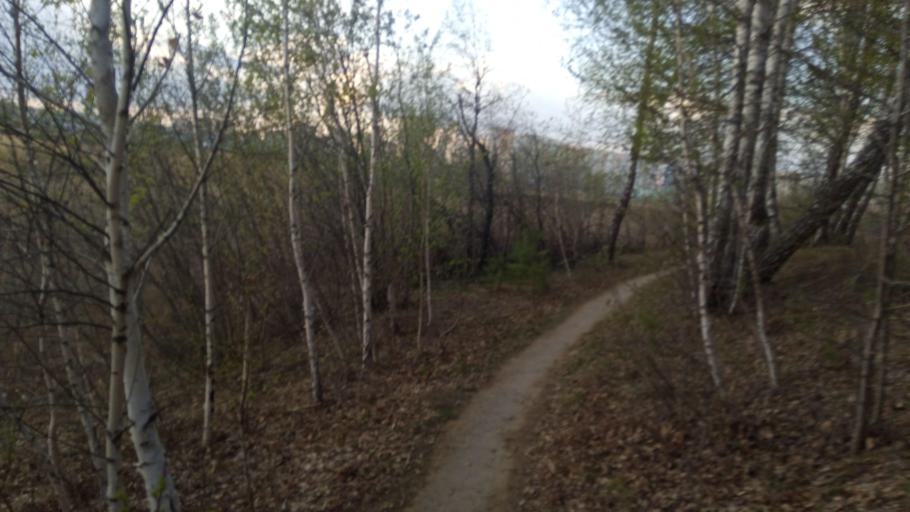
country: RU
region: Chelyabinsk
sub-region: Gorod Chelyabinsk
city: Chelyabinsk
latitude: 55.1625
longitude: 61.3126
